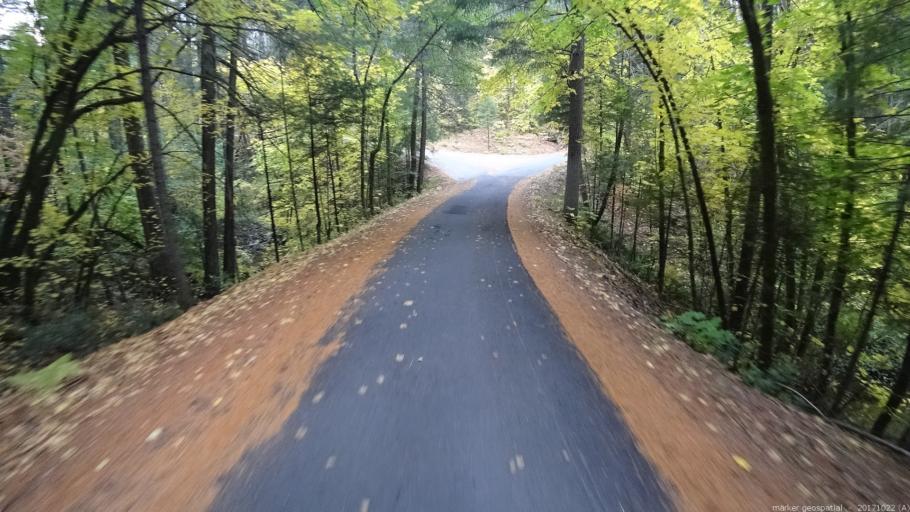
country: US
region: California
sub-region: Siskiyou County
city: Dunsmuir
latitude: 41.1526
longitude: -122.2892
